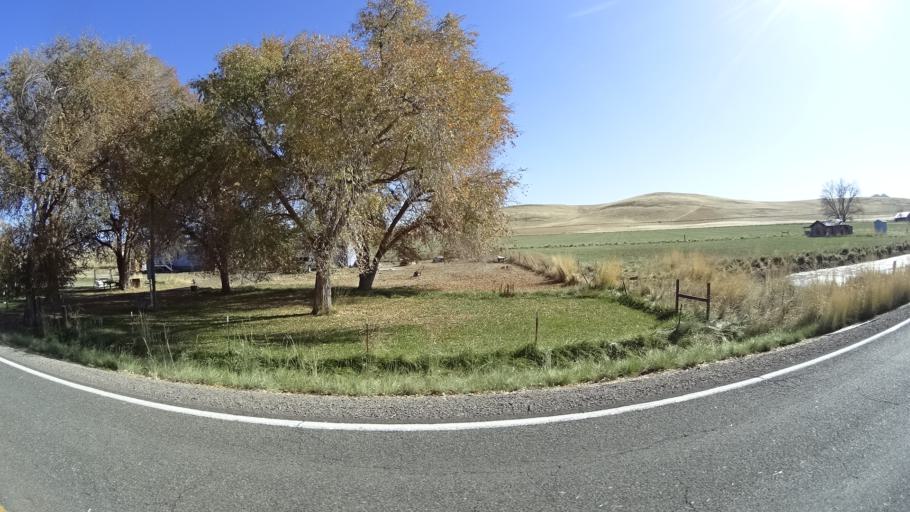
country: US
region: California
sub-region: Siskiyou County
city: Montague
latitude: 41.7444
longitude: -122.5077
